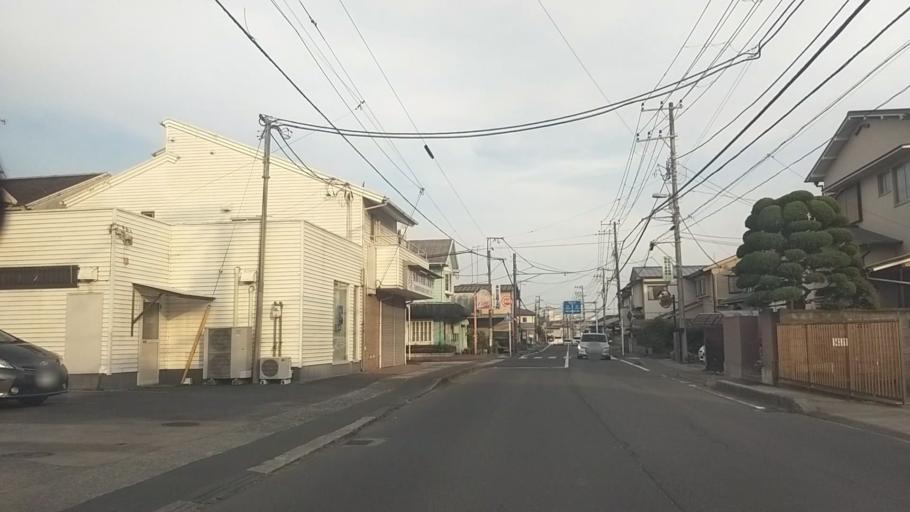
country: JP
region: Kanagawa
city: Odawara
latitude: 35.2738
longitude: 139.1579
